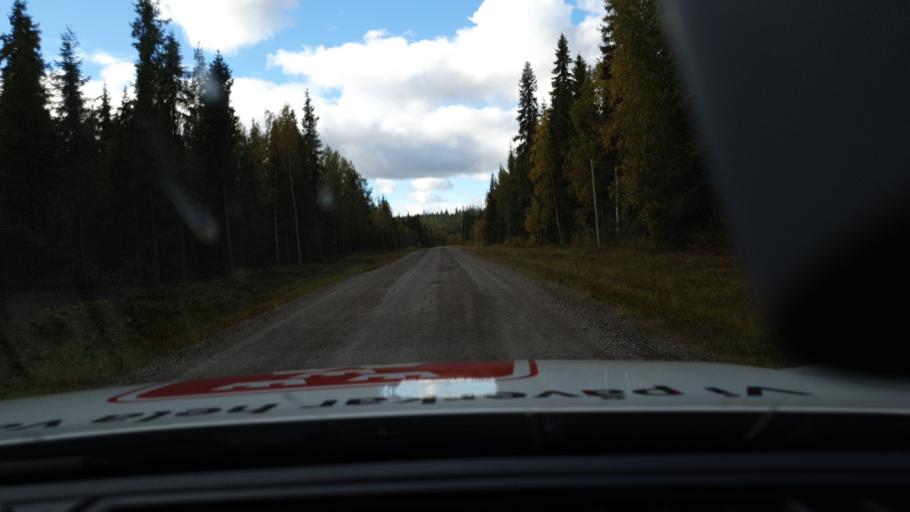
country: SE
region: Norrbotten
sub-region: Pajala Kommun
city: Pajala
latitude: 67.4436
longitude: 23.5051
